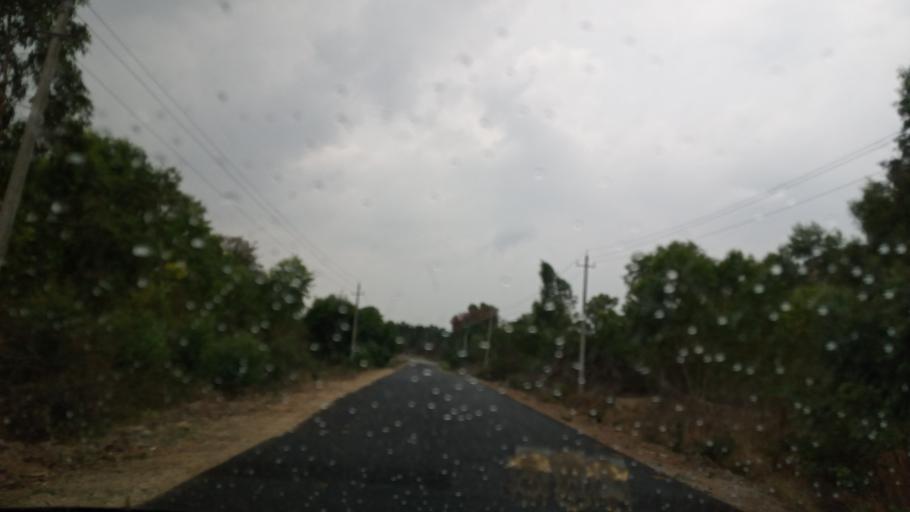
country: IN
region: Karnataka
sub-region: Kolar
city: Mulbagal
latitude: 13.1043
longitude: 78.3234
